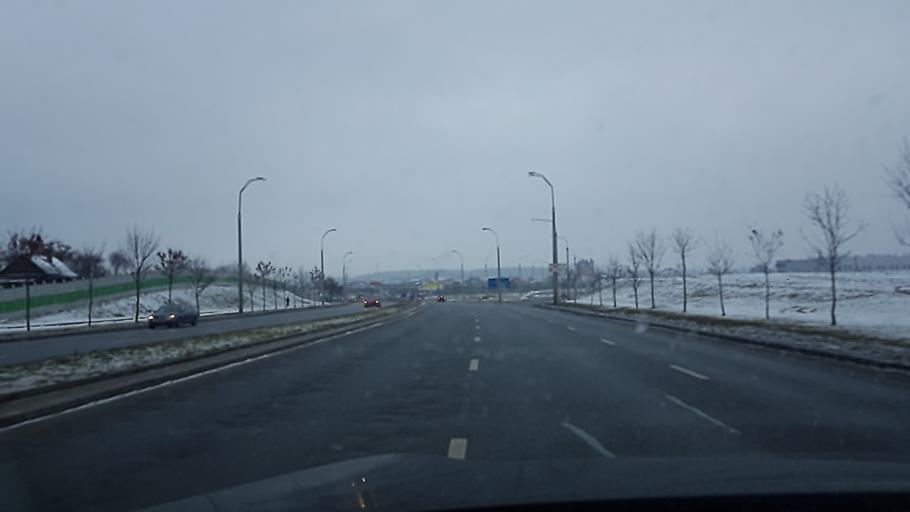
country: BY
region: Minsk
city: Bal'shavik
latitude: 53.9656
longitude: 27.5383
